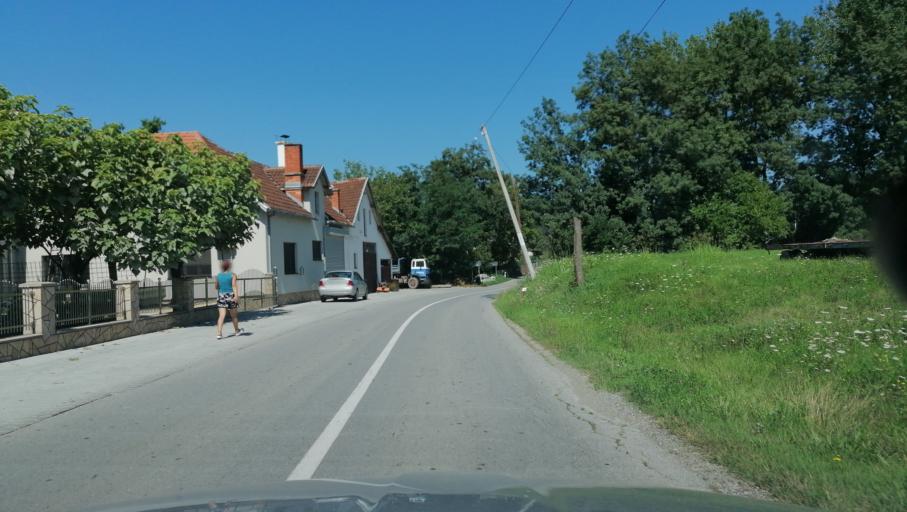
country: RS
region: Central Serbia
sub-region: Raski Okrug
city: Vrnjacka Banja
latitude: 43.6984
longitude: 20.8560
